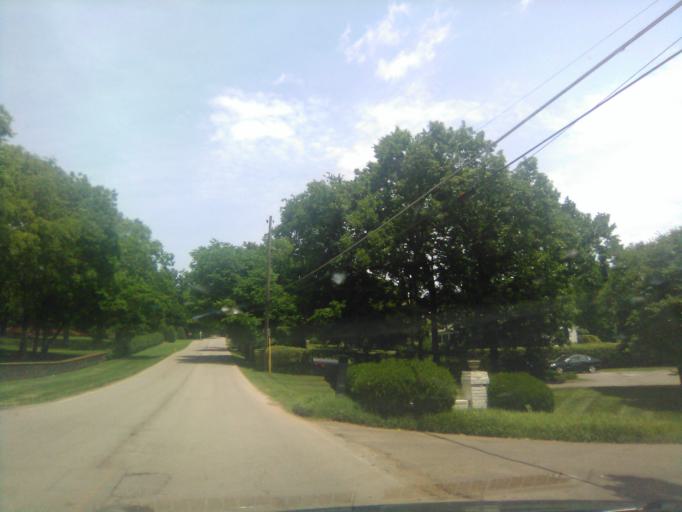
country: US
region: Tennessee
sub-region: Davidson County
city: Belle Meade
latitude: 36.0953
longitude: -86.8504
